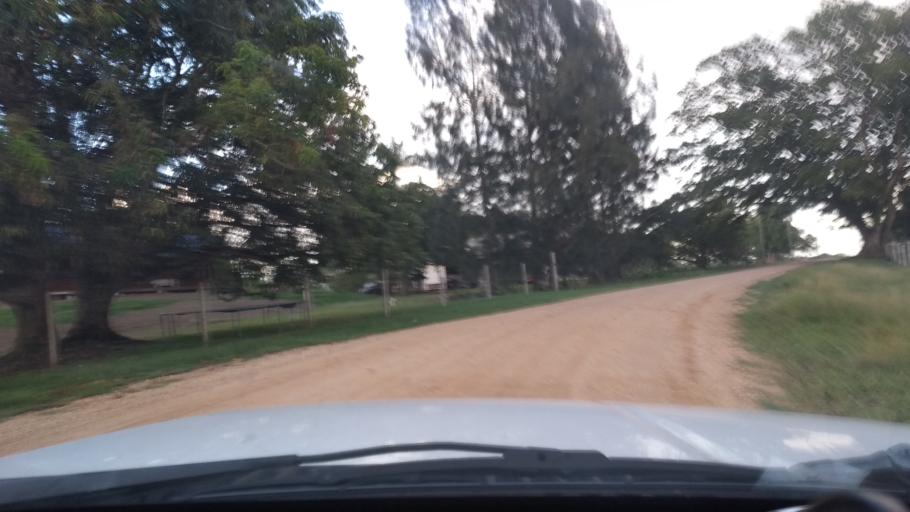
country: BZ
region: Cayo
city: San Ignacio
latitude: 17.2239
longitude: -88.9981
